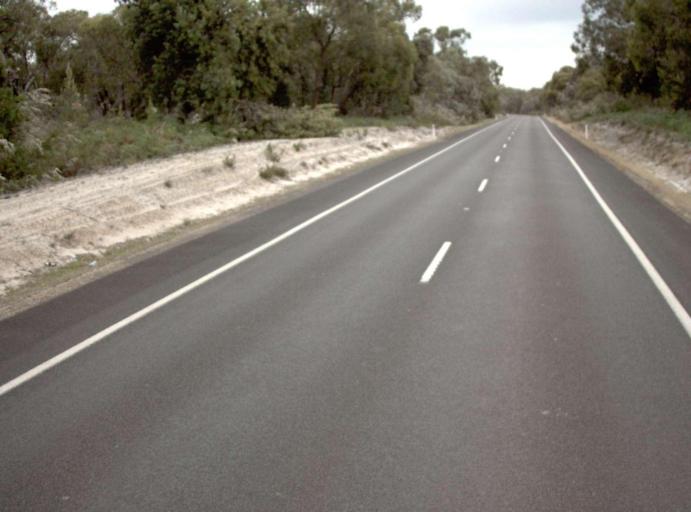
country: AU
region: Victoria
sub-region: Wellington
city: Sale
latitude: -38.3378
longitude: 147.0100
